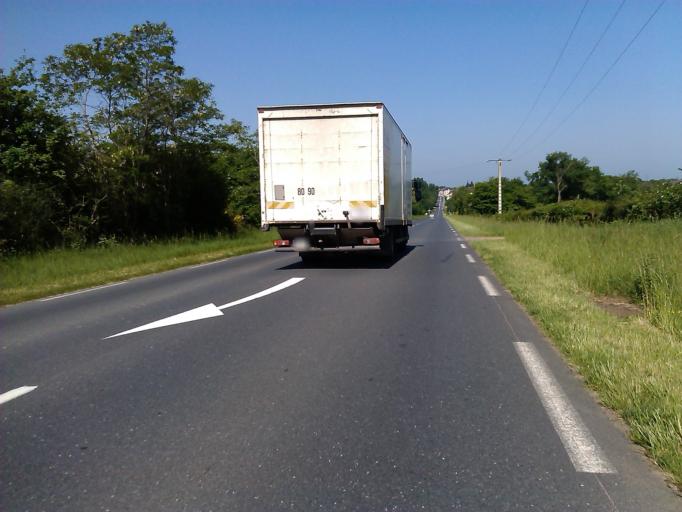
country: FR
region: Centre
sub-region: Departement de l'Indre
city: Arthon
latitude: 46.6120
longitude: 1.6962
